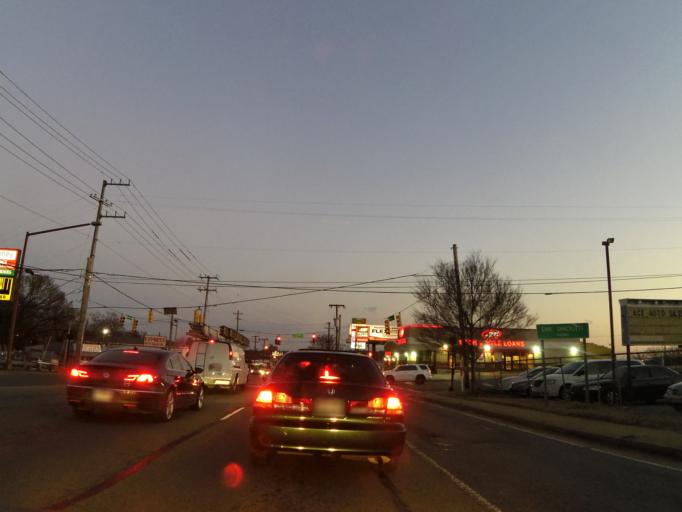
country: US
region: Tennessee
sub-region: Davidson County
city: Oak Hill
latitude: 36.1210
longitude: -86.7503
